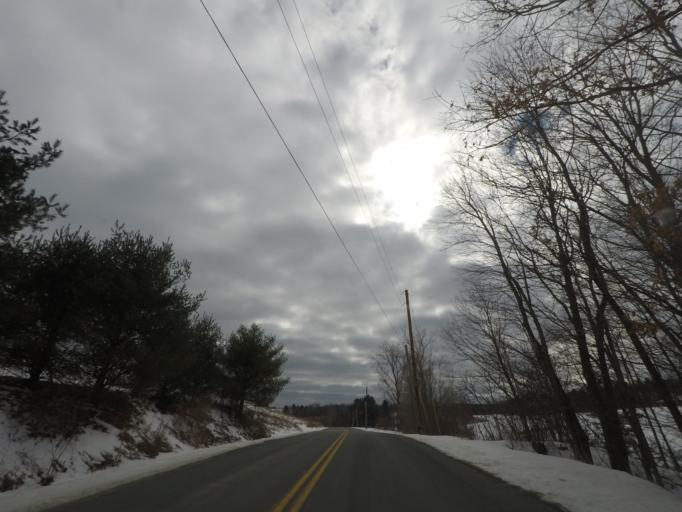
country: US
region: New York
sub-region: Rensselaer County
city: Hoosick Falls
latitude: 42.8778
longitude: -73.4126
